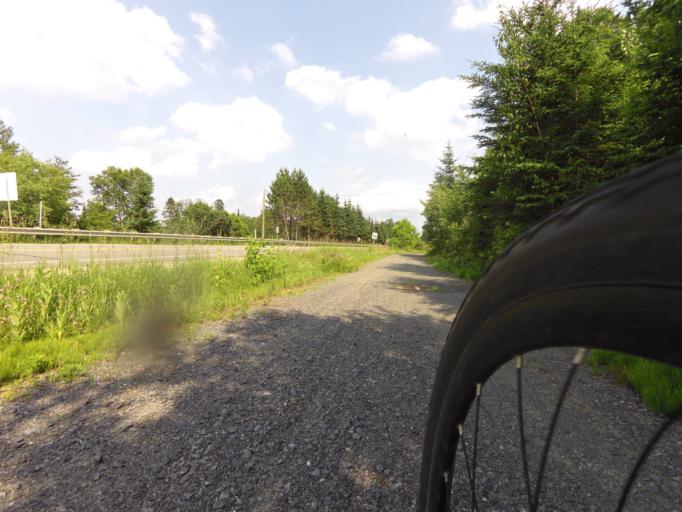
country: CA
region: Quebec
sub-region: Laurentides
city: Mont-Tremblant
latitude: 45.9657
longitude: -74.6139
